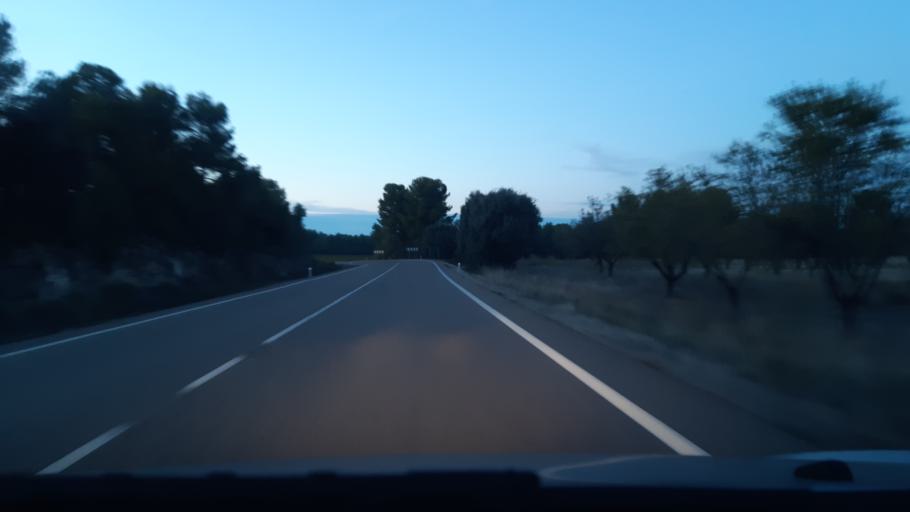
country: ES
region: Aragon
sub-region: Provincia de Teruel
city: Lledo
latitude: 40.9526
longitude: 0.2232
